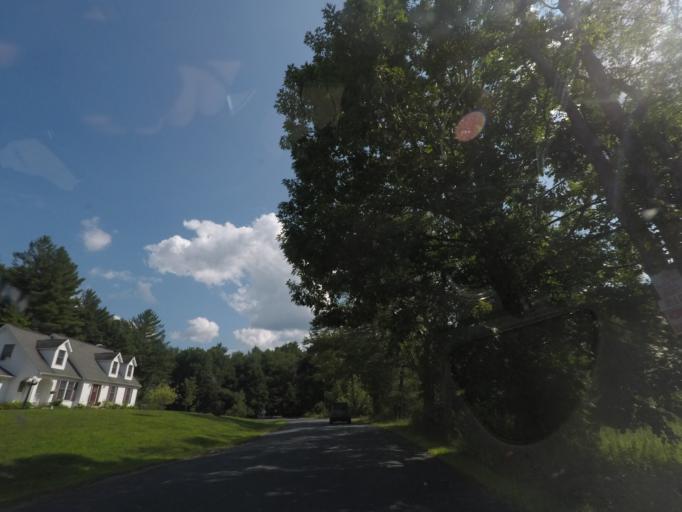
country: US
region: New York
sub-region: Rensselaer County
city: West Sand Lake
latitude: 42.6404
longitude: -73.5930
